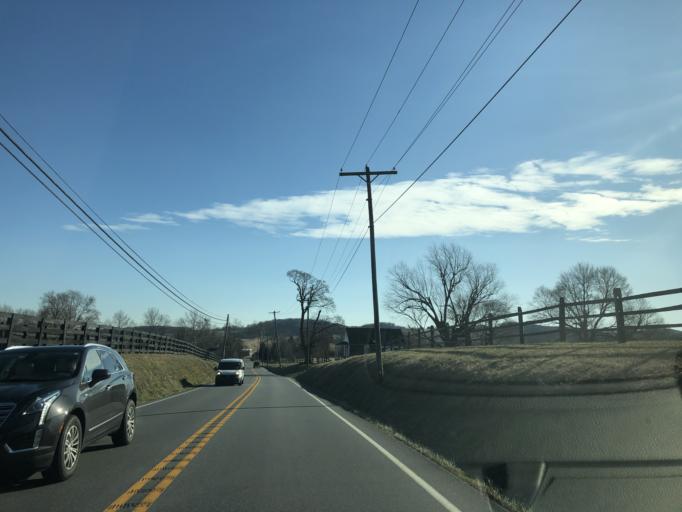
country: US
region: Pennsylvania
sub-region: Chester County
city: South Coatesville
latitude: 39.9202
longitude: -75.8210
